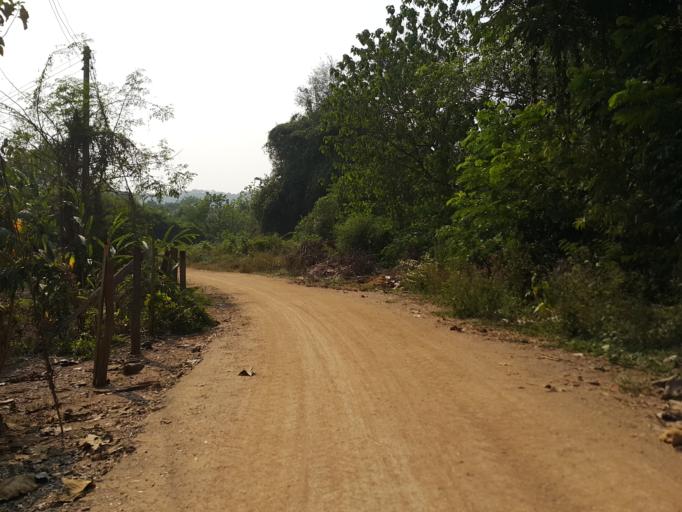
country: TH
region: Sukhothai
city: Thung Saliam
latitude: 17.3315
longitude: 99.4797
